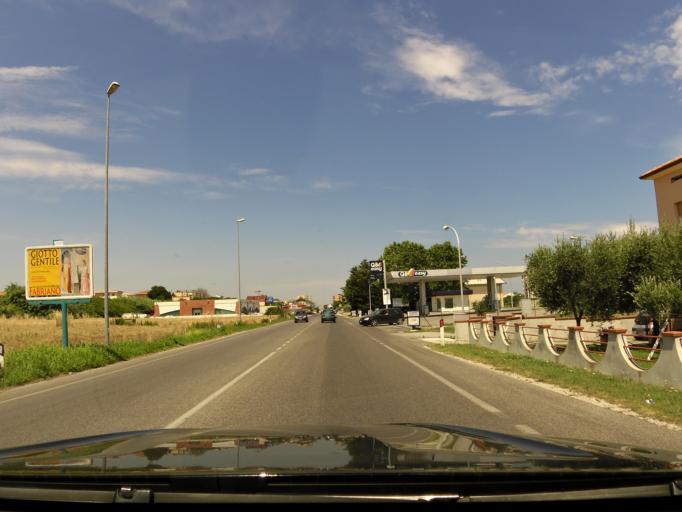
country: IT
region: The Marches
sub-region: Provincia di Pesaro e Urbino
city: Marotta
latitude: 43.7563
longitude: 13.1581
